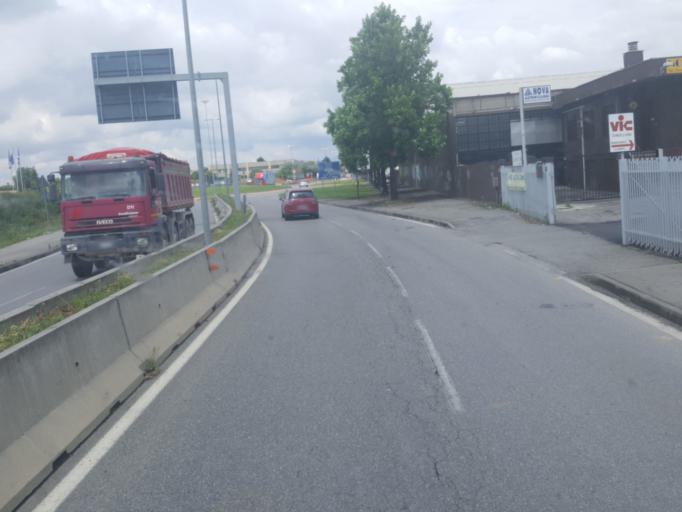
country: IT
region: Lombardy
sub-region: Provincia di Monza e Brianza
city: Nova Milanese
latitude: 45.5781
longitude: 9.2077
